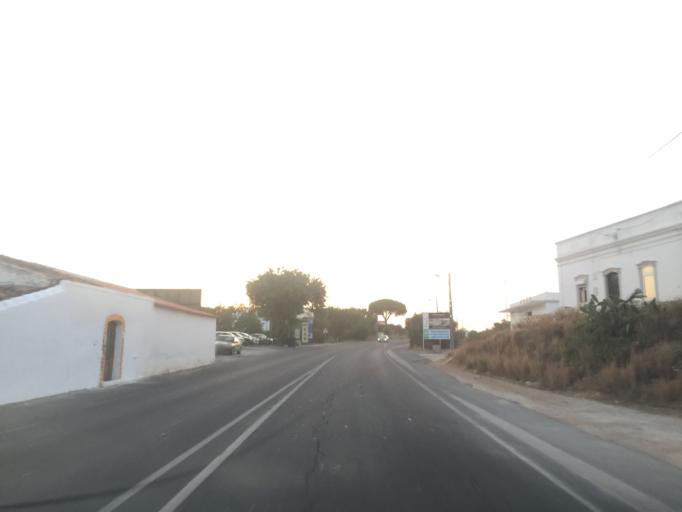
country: PT
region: Faro
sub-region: Faro
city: Santa Barbara de Nexe
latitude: 37.0773
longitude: -7.9889
